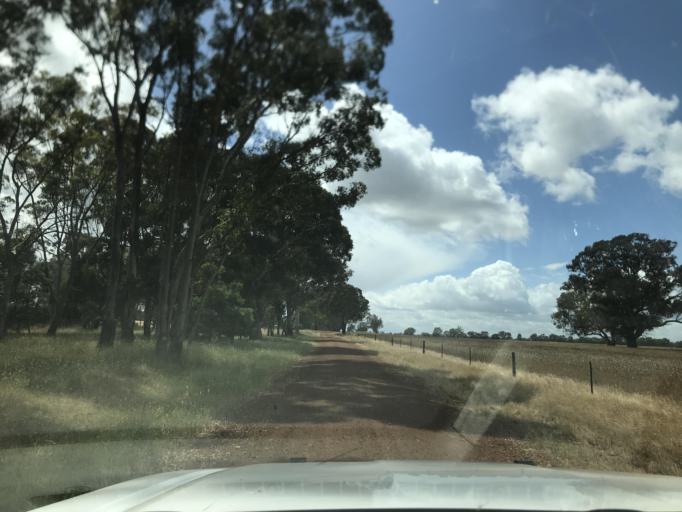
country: AU
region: South Australia
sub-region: Wattle Range
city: Penola
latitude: -37.1818
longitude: 141.4464
